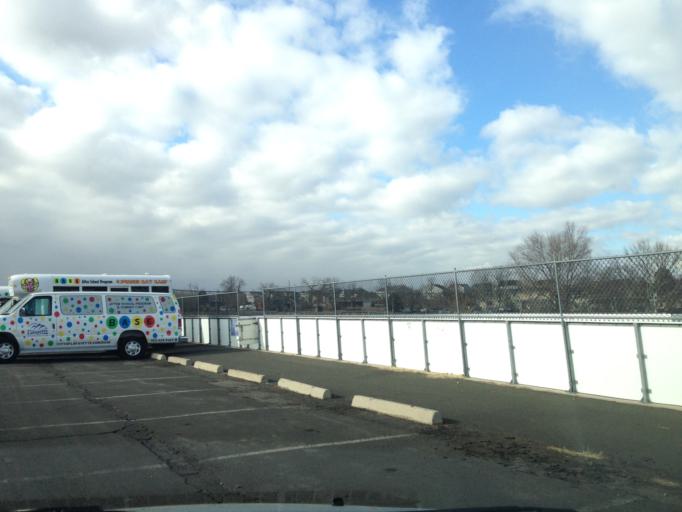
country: US
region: Colorado
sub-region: Boulder County
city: Lafayette
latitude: 40.0023
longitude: -105.0908
